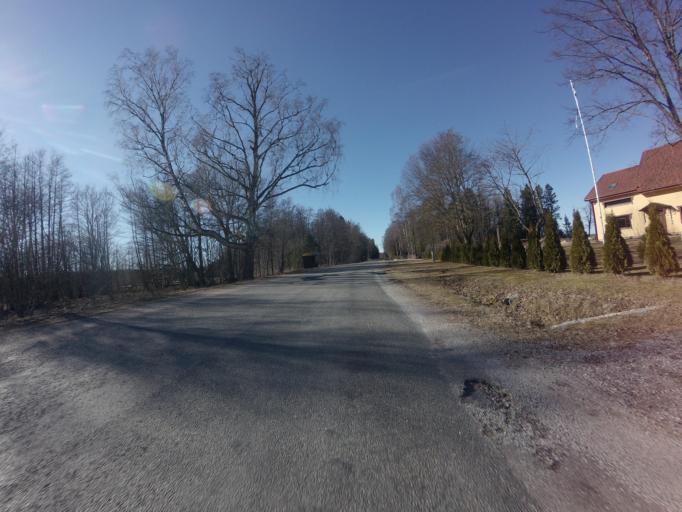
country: EE
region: Saare
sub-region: Kuressaare linn
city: Kuressaare
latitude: 58.5750
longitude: 22.6460
